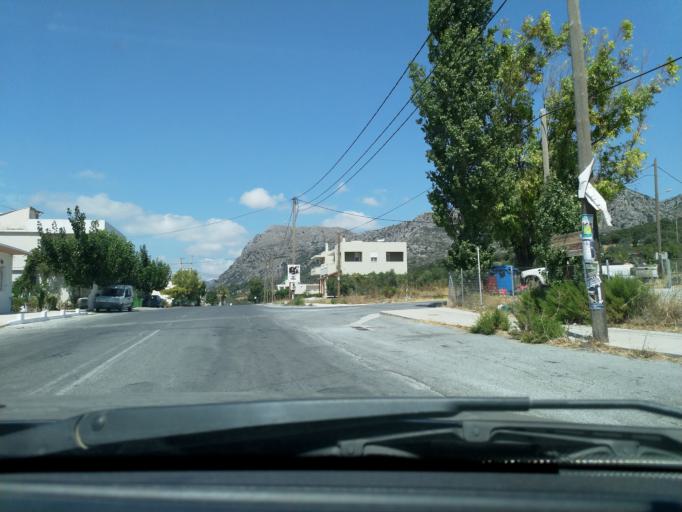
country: GR
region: Crete
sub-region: Nomos Rethymnis
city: Agia Foteini
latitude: 35.1873
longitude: 24.5543
